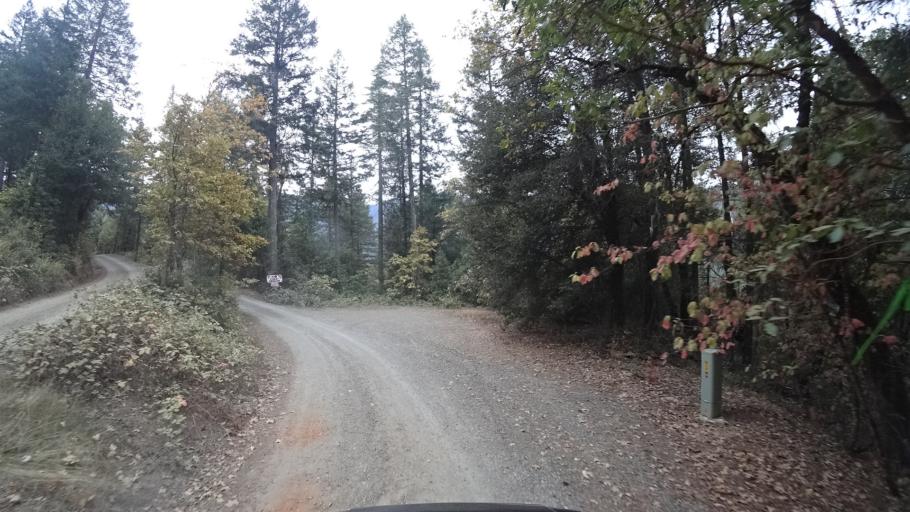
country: US
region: California
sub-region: Siskiyou County
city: Happy Camp
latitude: 41.7865
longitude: -123.3359
